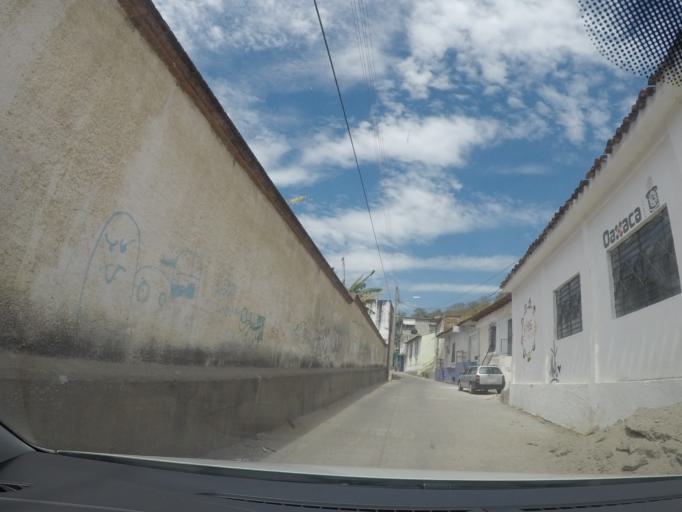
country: MX
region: Oaxaca
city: San Blas Atempa
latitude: 16.3333
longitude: -95.2309
